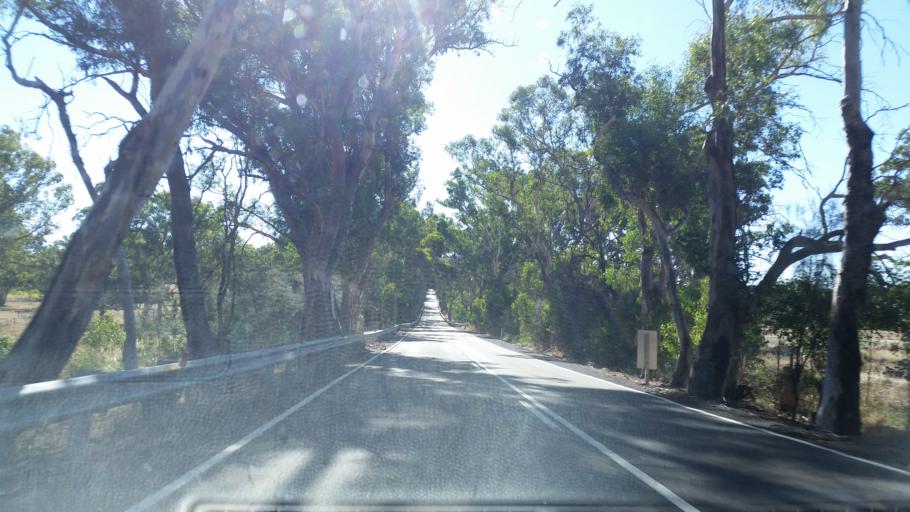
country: AU
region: South Australia
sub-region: Adelaide Hills
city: Birdwood
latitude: -34.8147
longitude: 139.0402
